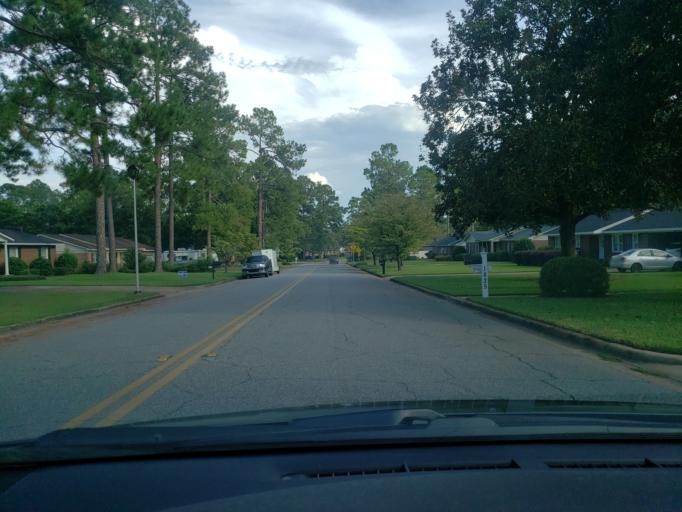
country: US
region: Georgia
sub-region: Dougherty County
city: Albany
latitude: 31.5902
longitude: -84.2041
